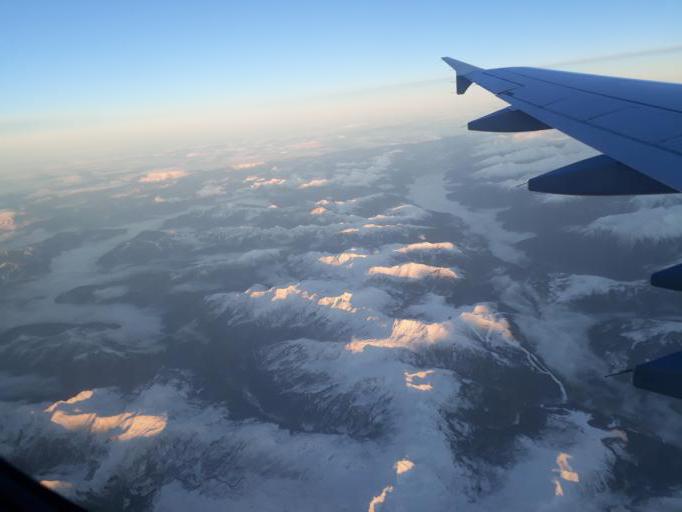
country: AT
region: Tyrol
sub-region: Politischer Bezirk Schwaz
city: Stummerberg
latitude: 47.2624
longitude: 11.9059
